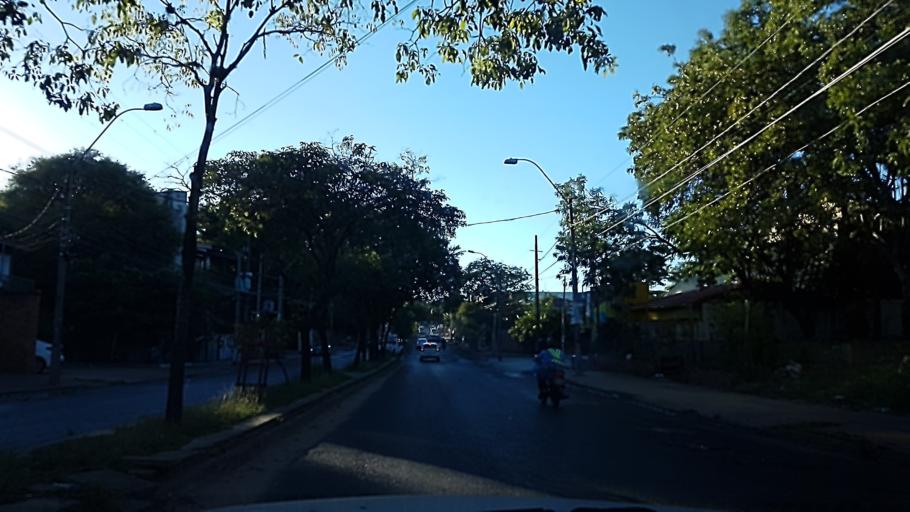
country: PY
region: Asuncion
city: Asuncion
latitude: -25.2684
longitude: -57.5654
